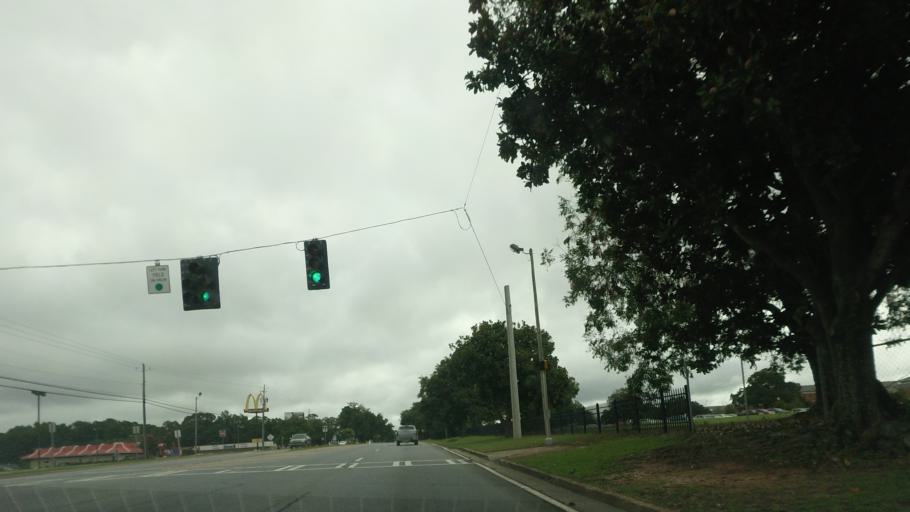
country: US
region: Georgia
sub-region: Laurens County
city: Dublin
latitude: 32.5398
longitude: -82.9444
